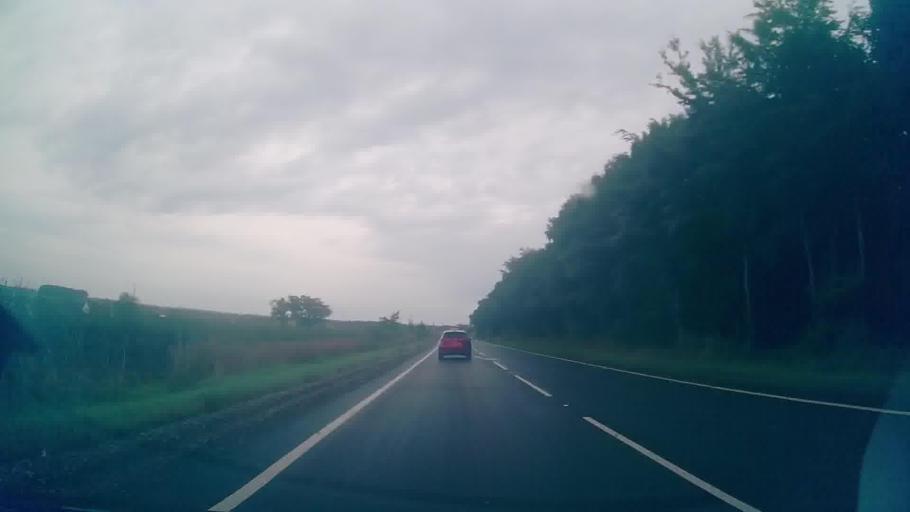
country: GB
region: Scotland
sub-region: Dumfries and Galloway
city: Annan
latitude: 55.0006
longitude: -3.3032
